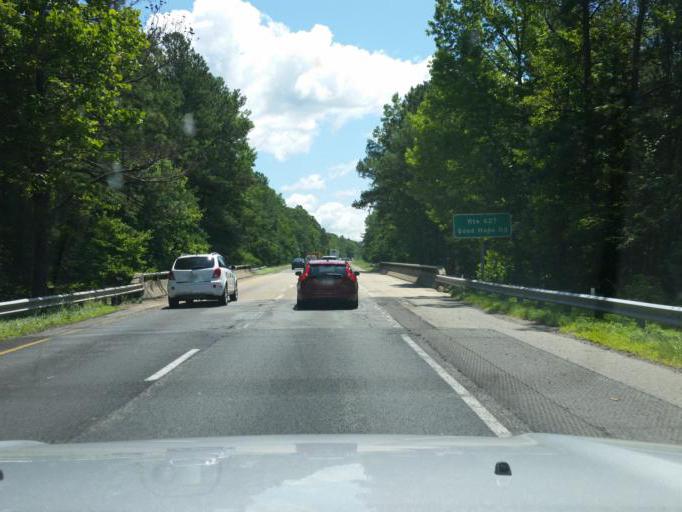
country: US
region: Virginia
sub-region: New Kent County
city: New Kent
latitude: 37.4822
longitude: -76.9353
